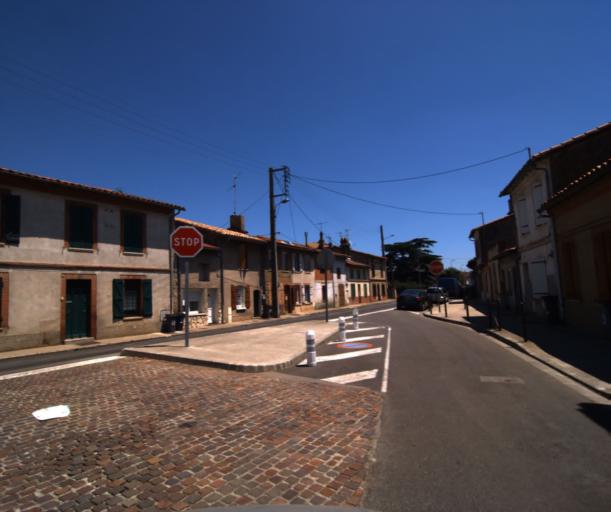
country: FR
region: Midi-Pyrenees
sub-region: Departement de la Haute-Garonne
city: Muret
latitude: 43.4628
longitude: 1.3207
